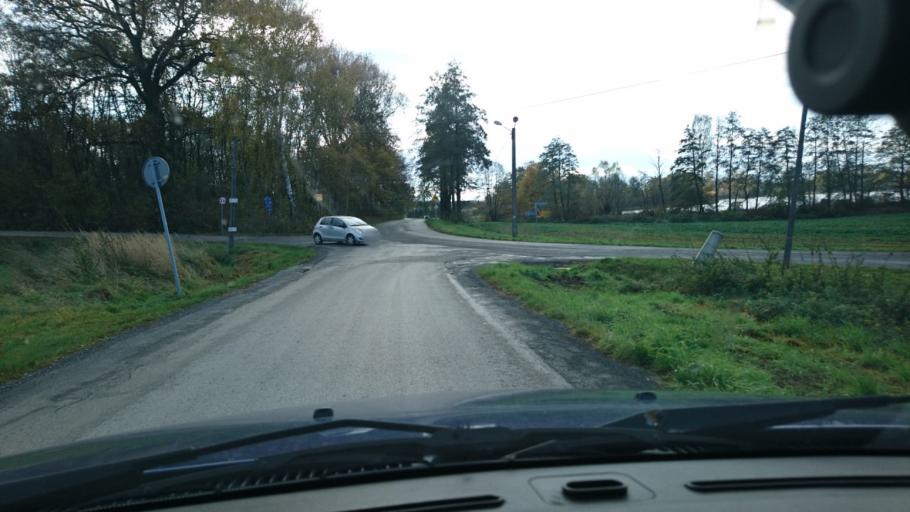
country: PL
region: Lesser Poland Voivodeship
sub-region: Powiat oswiecimski
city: Malec
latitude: 49.9393
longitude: 19.2318
